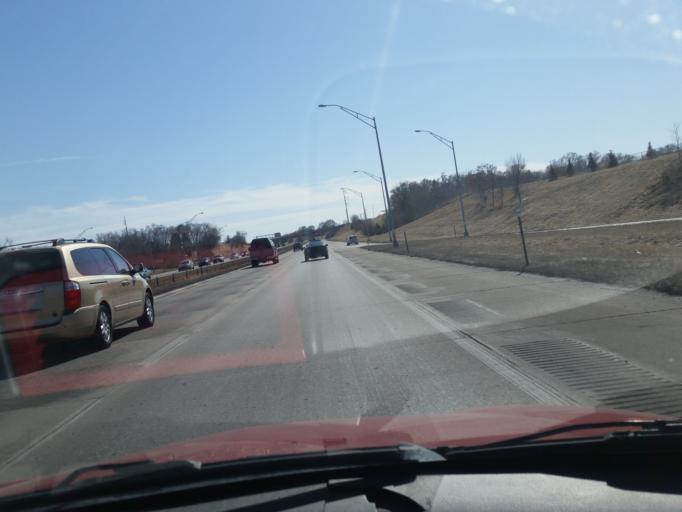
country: US
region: Nebraska
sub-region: Sarpy County
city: Offutt Air Force Base
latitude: 41.1822
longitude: -95.9386
